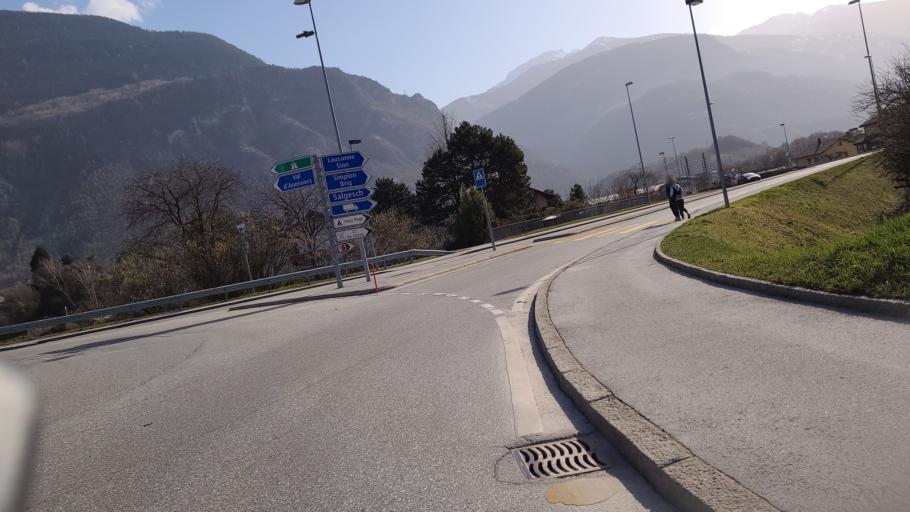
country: CH
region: Valais
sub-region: Sierre District
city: Veyras
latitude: 46.2979
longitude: 7.5504
